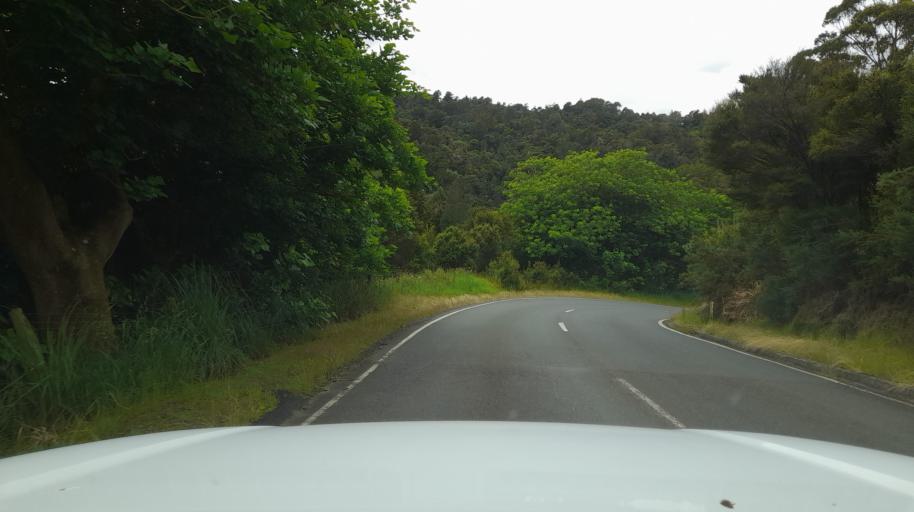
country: NZ
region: Northland
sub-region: Far North District
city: Kaitaia
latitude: -35.3564
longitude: 173.4646
